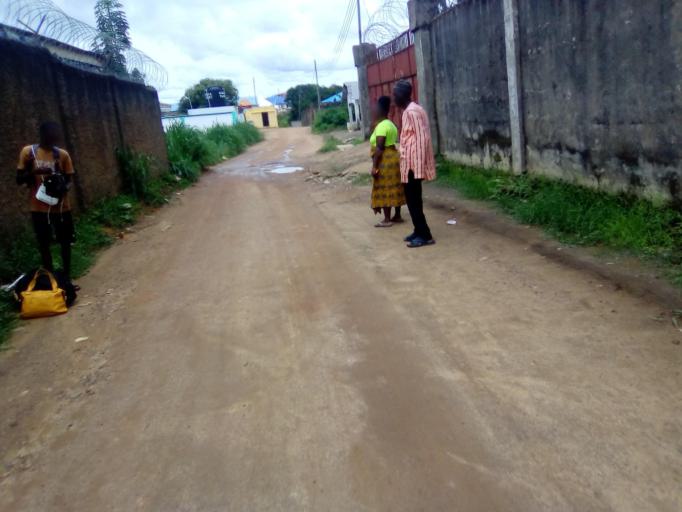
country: SL
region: Southern Province
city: Bo
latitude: 7.9477
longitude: -11.7114
